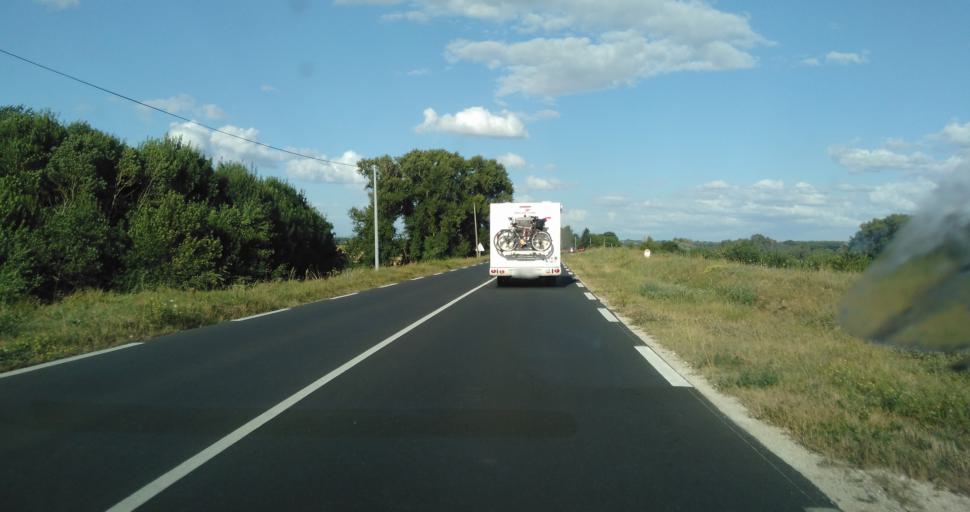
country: FR
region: Centre
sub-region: Departement d'Indre-et-Loire
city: Noizay
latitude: 47.4045
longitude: 0.9248
